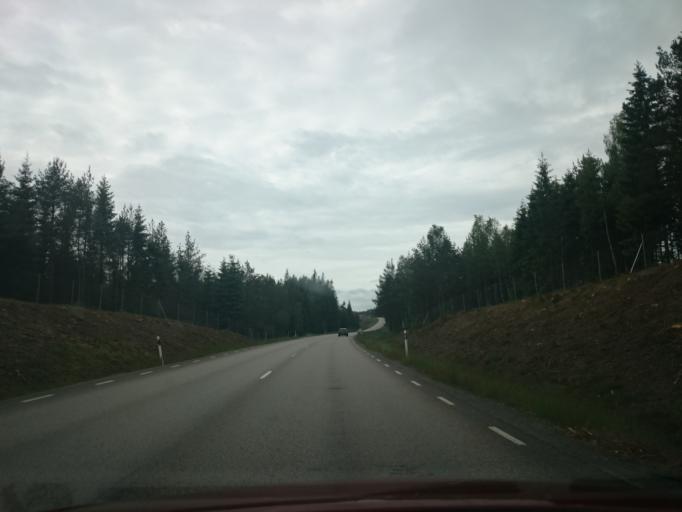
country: SE
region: Vaestra Goetaland
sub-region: Harryda Kommun
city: Hindas
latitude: 57.6852
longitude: 12.3675
